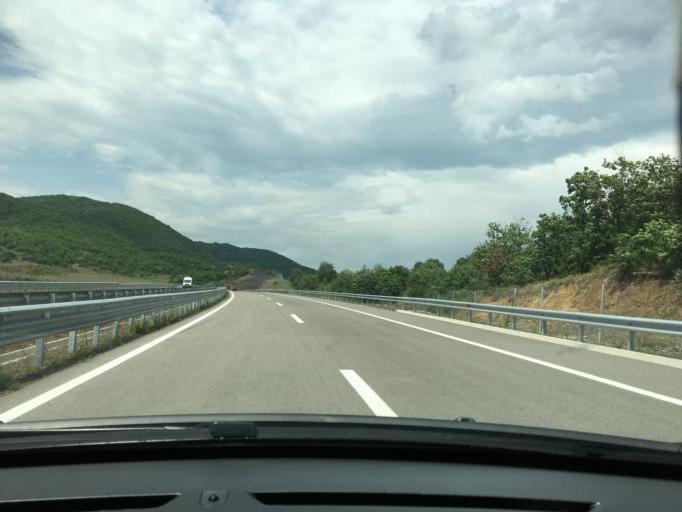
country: MK
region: Gevgelija
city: Miravci
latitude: 41.3349
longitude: 22.3886
